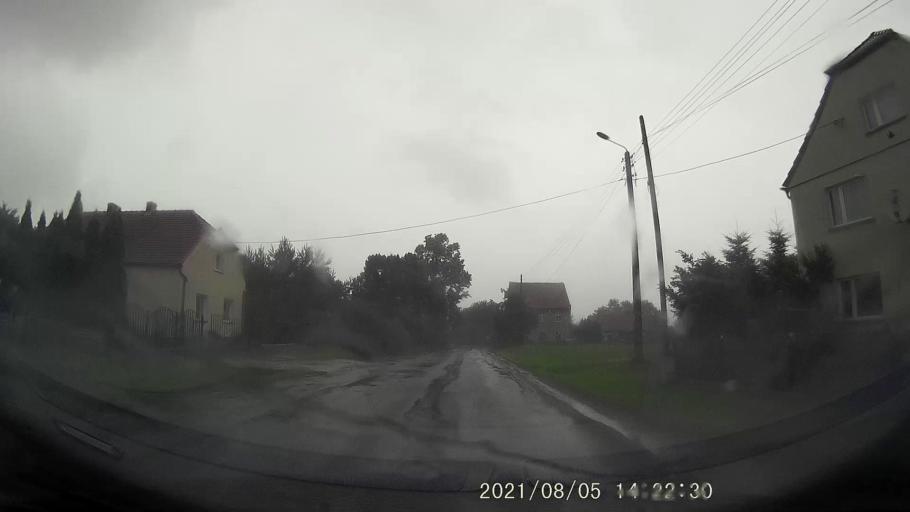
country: PL
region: Opole Voivodeship
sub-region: Powiat nyski
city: Korfantow
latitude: 50.4774
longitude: 17.6562
